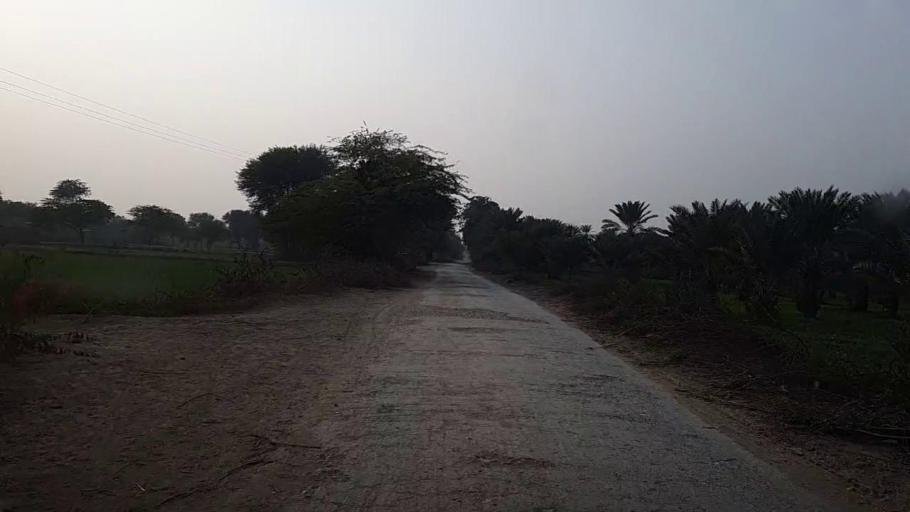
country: PK
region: Sindh
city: Setharja Old
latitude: 27.0810
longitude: 68.5228
